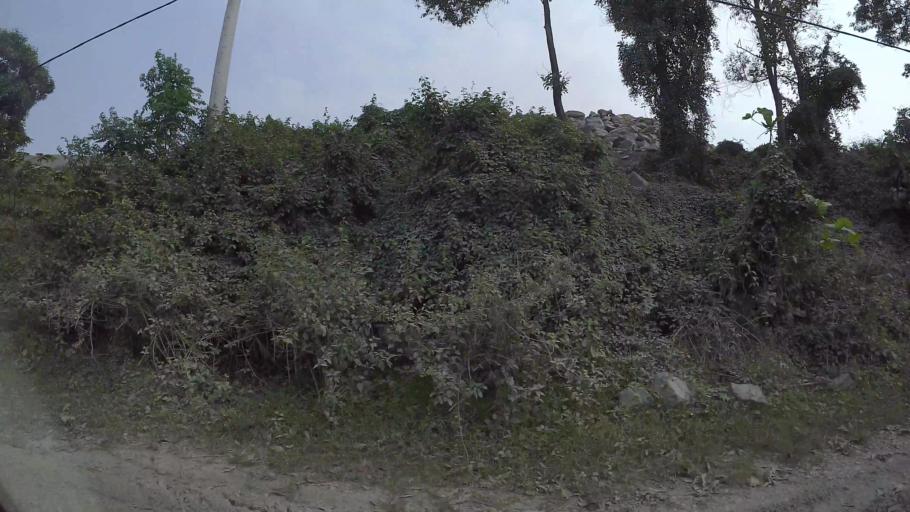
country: VN
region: Da Nang
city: Lien Chieu
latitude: 16.0442
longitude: 108.1477
